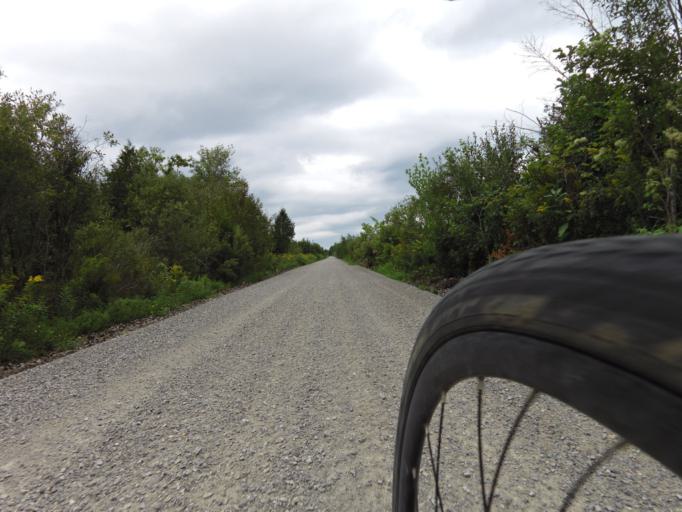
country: CA
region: Ontario
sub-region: Lanark County
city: Smiths Falls
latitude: 44.9479
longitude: -76.0428
